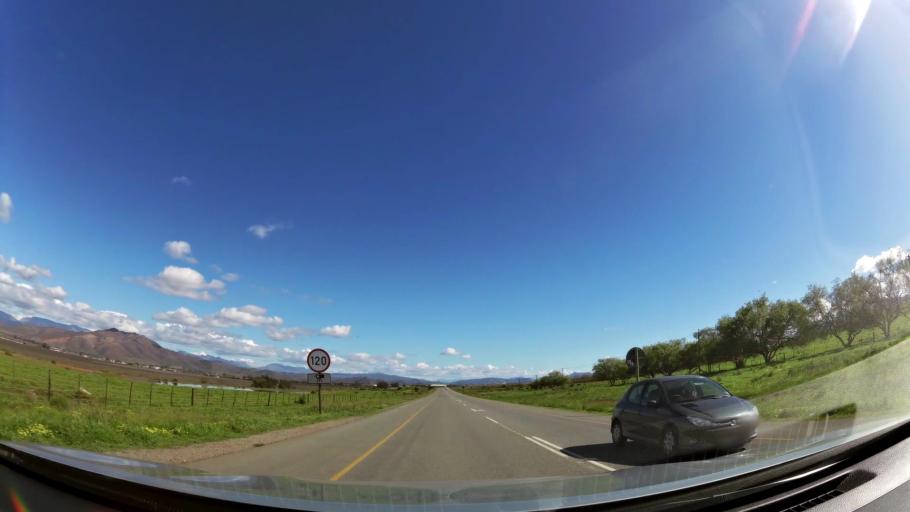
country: ZA
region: Western Cape
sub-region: Cape Winelands District Municipality
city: Ashton
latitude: -33.8383
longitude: 20.0276
